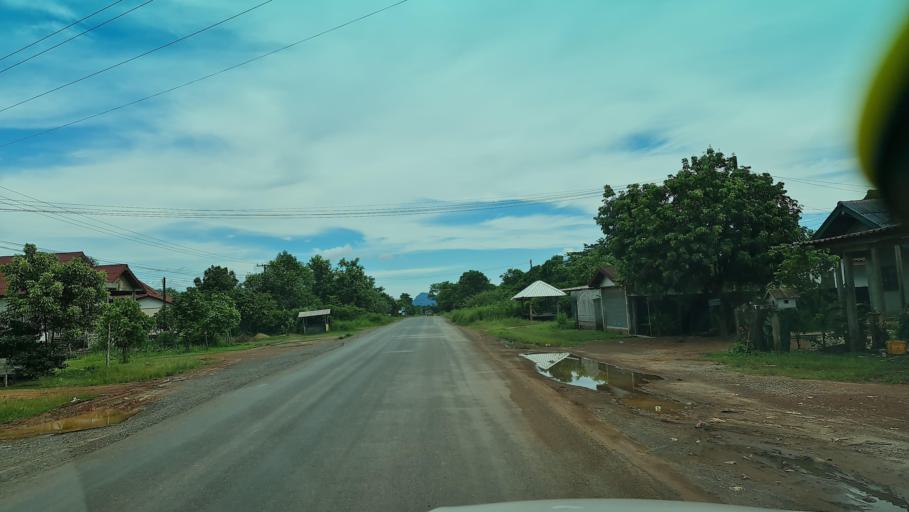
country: LA
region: Bolikhamxai
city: Ban Nahin
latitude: 18.1165
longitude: 104.2727
